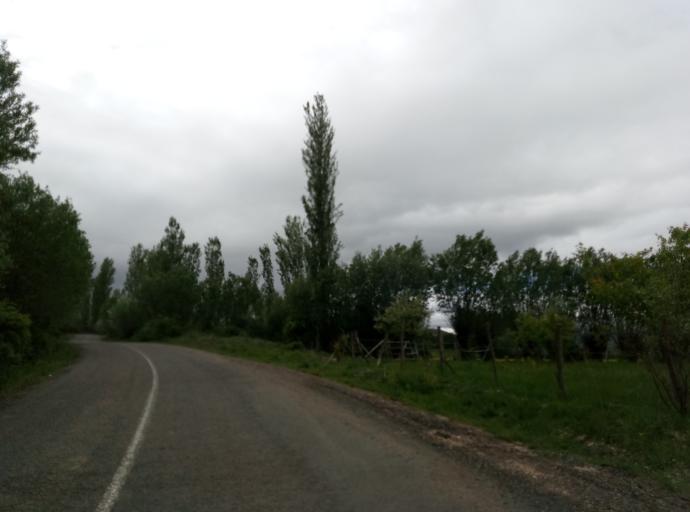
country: TR
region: Sivas
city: Susehri
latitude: 40.1878
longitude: 38.0157
